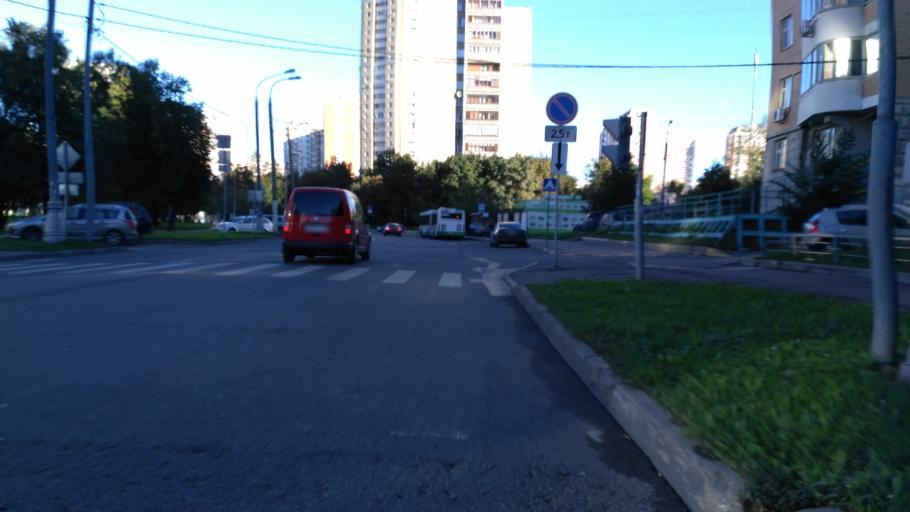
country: RU
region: Moskovskaya
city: Vostochnoe Degunino
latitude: 55.8719
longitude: 37.5546
